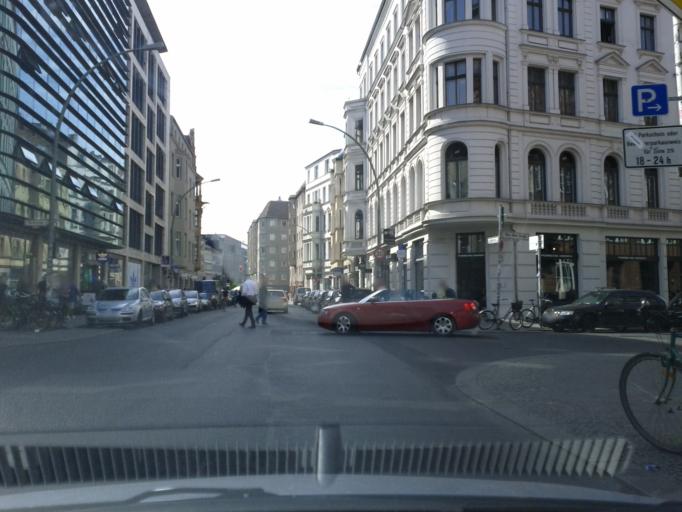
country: DE
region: Berlin
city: Berlin
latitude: 52.5245
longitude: 13.4081
